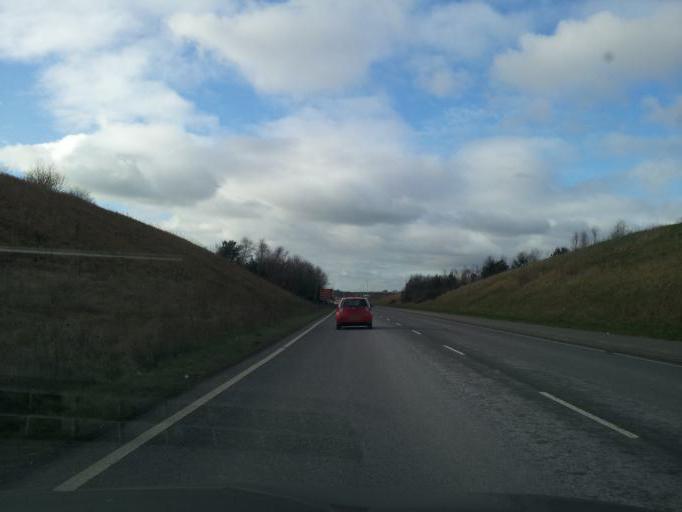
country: GB
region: England
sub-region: Nottinghamshire
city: Mansfield
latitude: 53.1222
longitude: -1.2098
